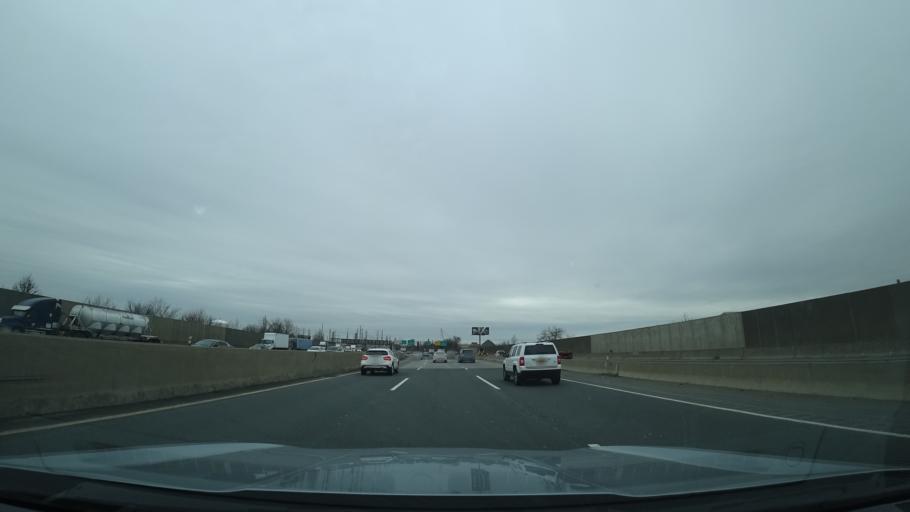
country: US
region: New Jersey
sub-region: Union County
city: Elizabeth
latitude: 40.6514
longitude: -74.1984
